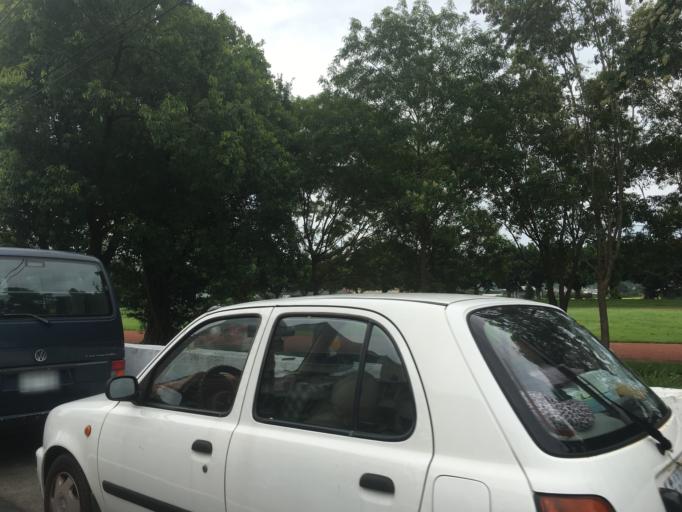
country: TW
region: Taiwan
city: Zhongxing New Village
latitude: 24.0489
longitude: 120.6867
